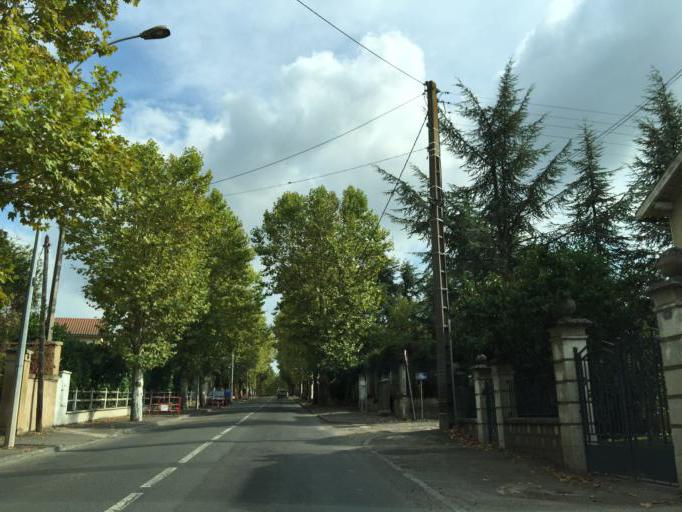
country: FR
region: Rhone-Alpes
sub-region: Departement de la Loire
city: Sury-le-Comtal
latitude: 45.5352
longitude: 4.1923
